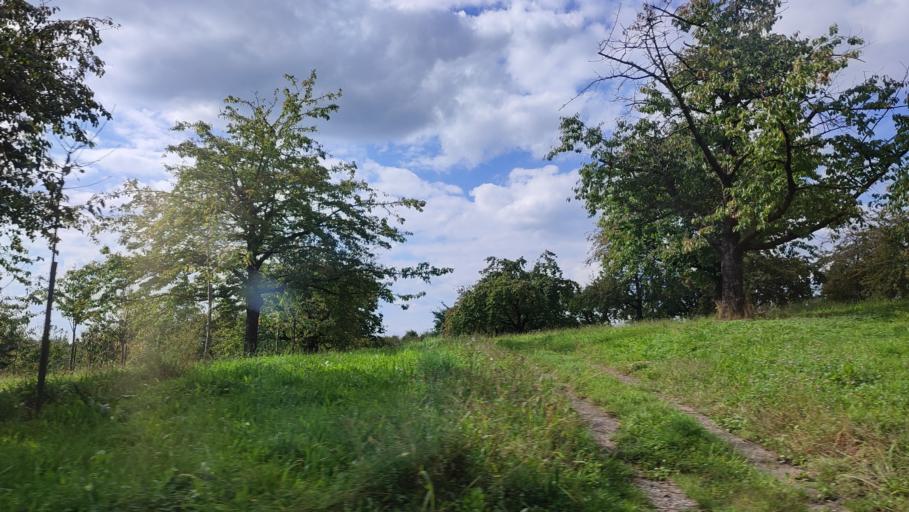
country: DE
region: Baden-Wuerttemberg
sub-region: Freiburg Region
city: Appenweier
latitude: 48.5239
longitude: 8.0063
